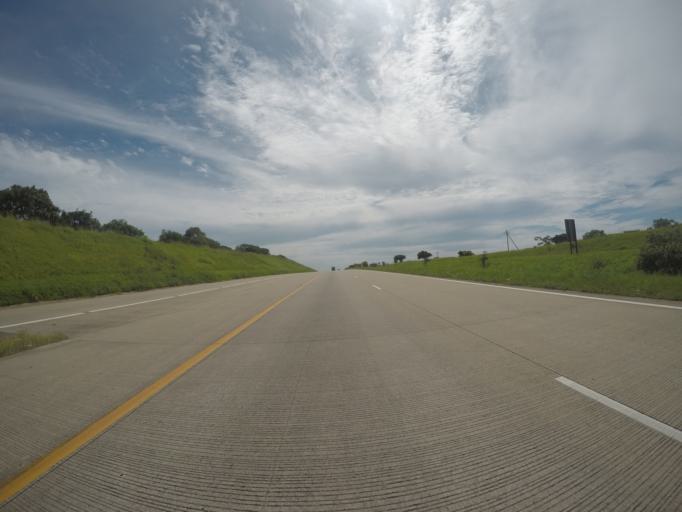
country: ZA
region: KwaZulu-Natal
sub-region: iLembe District Municipality
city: Stanger
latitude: -29.3438
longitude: 31.3266
